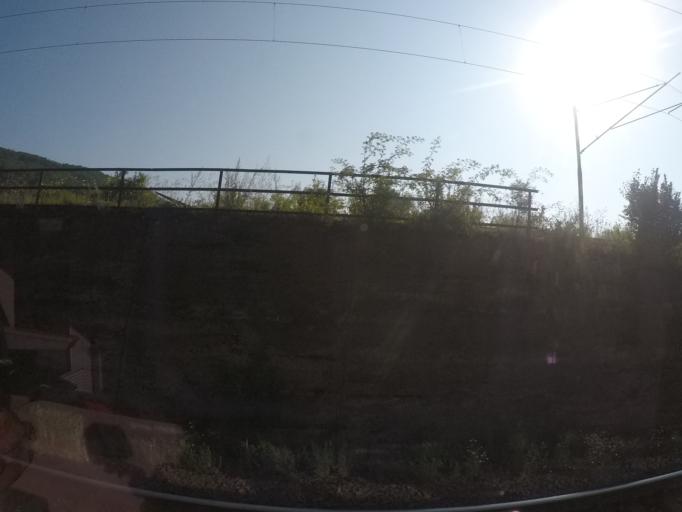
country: SK
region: Presovsky
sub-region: Okres Presov
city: Presov
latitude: 48.8593
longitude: 21.2221
